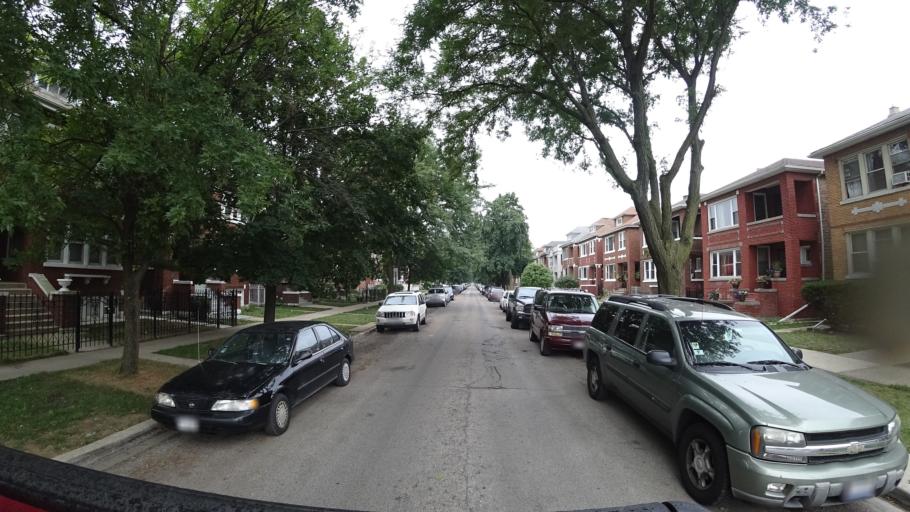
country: US
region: Illinois
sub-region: Cook County
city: Cicero
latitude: 41.8584
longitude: -87.7482
